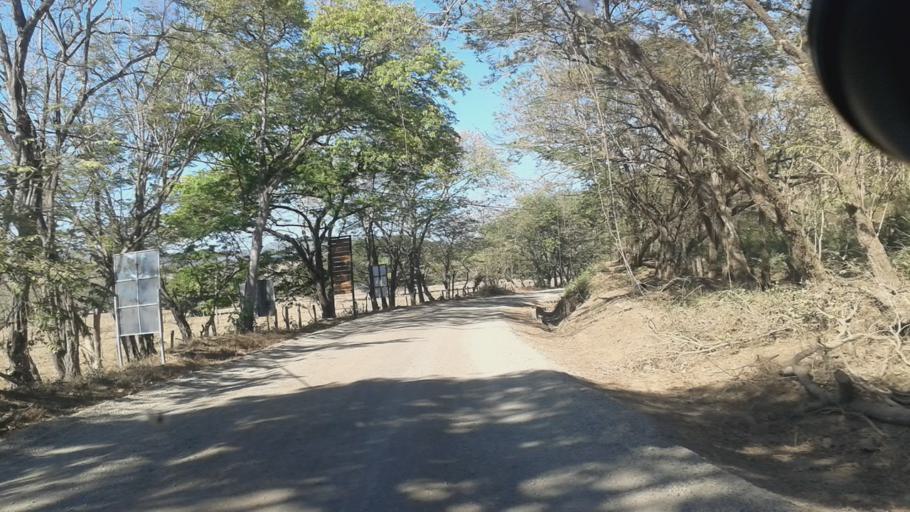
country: CR
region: Guanacaste
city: Samara
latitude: 9.9010
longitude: -85.5864
